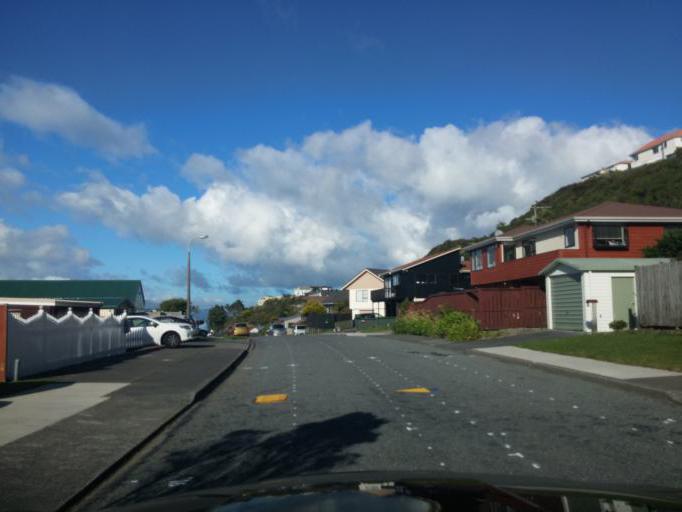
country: NZ
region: Wellington
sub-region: Wellington City
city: Wellington
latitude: -41.2322
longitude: 174.7919
